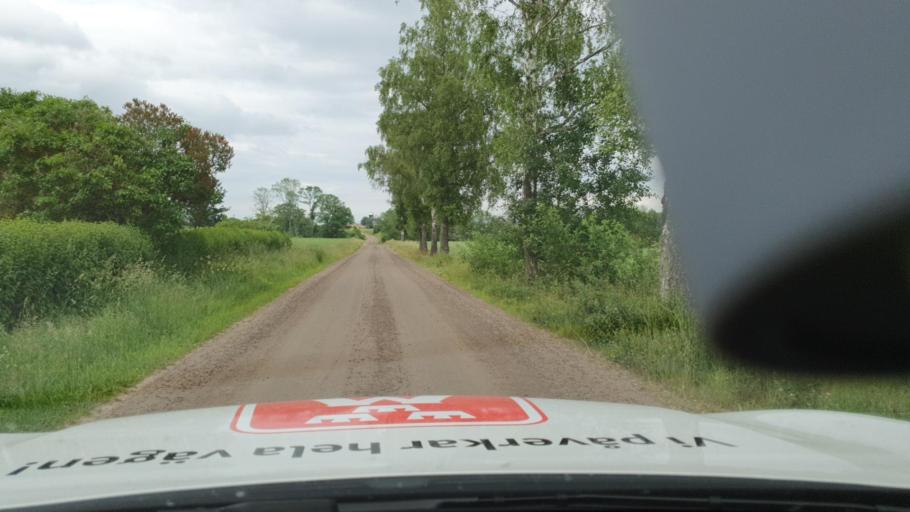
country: SE
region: Vaestra Goetaland
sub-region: Hjo Kommun
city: Hjo
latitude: 58.2075
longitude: 14.1789
